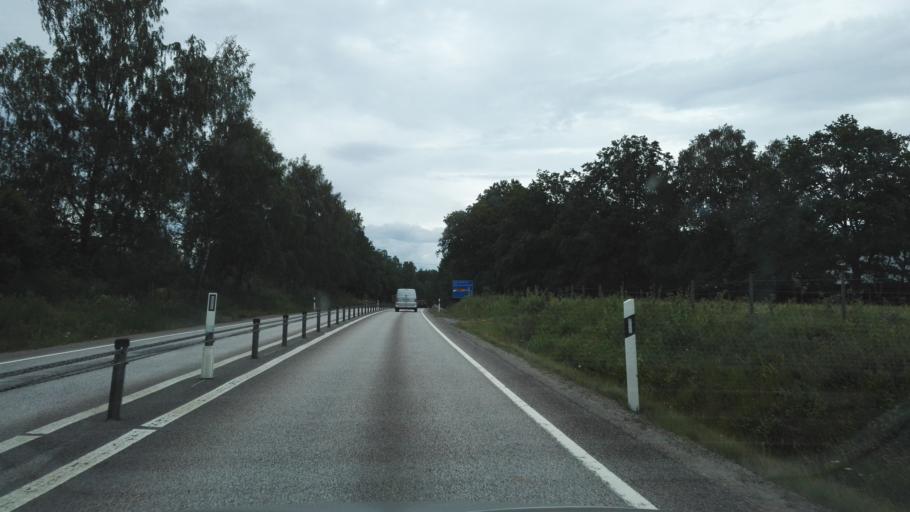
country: SE
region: Kronoberg
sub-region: Vaxjo Kommun
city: Rottne
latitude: 56.9828
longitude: 14.9852
